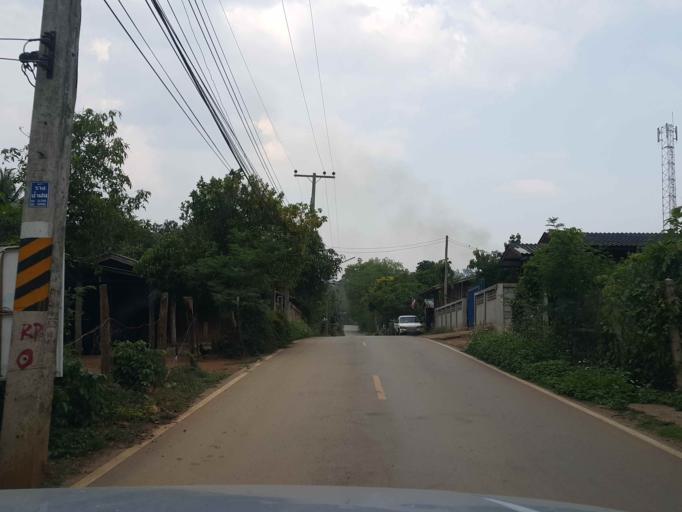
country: TH
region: Chiang Mai
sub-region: Amphoe Chiang Dao
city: Chiang Dao
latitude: 19.3874
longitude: 98.9306
